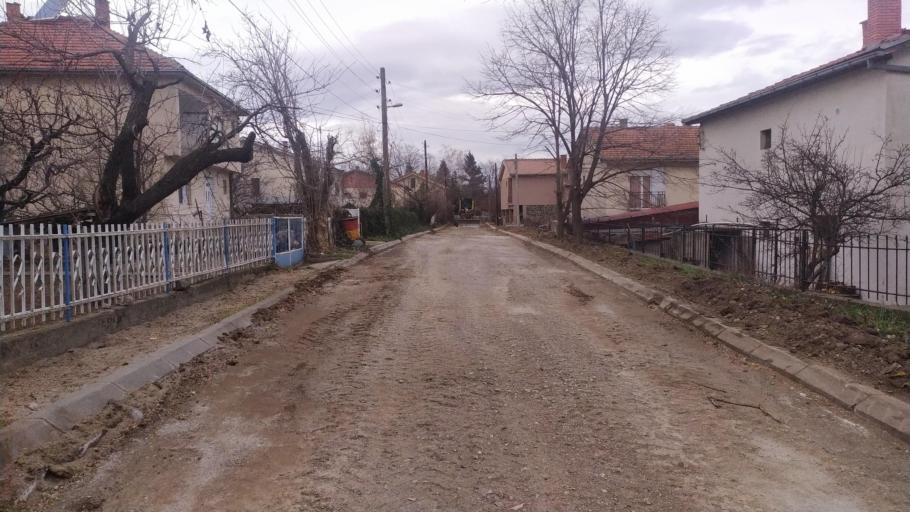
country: MK
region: Demir Kapija
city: Demir Kapija
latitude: 41.4134
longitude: 22.2390
